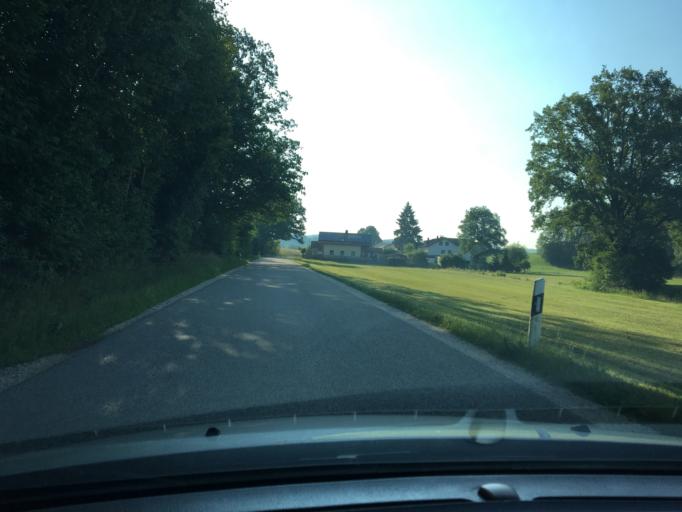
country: DE
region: Bavaria
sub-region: Lower Bavaria
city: Vilsbiburg
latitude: 48.4383
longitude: 12.3332
